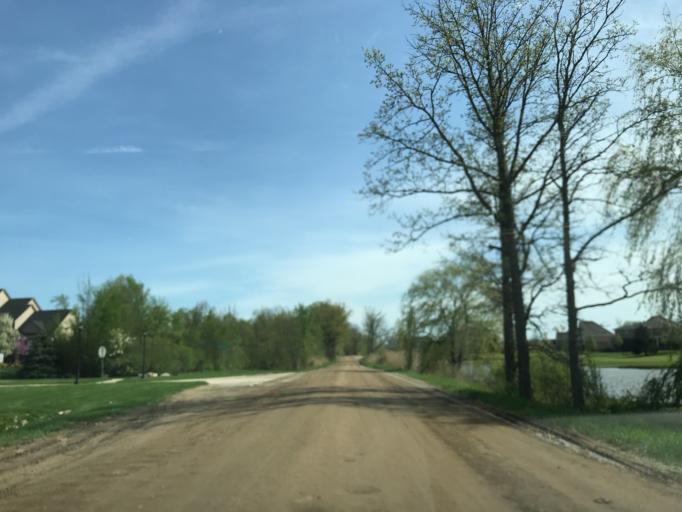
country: US
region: Michigan
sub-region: Oakland County
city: Wixom
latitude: 42.4610
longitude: -83.5732
